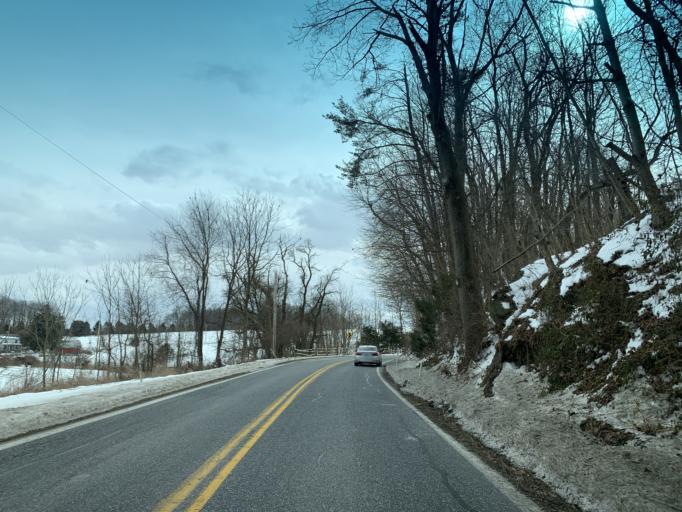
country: US
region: Pennsylvania
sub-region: York County
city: Shrewsbury
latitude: 39.8099
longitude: -76.6289
